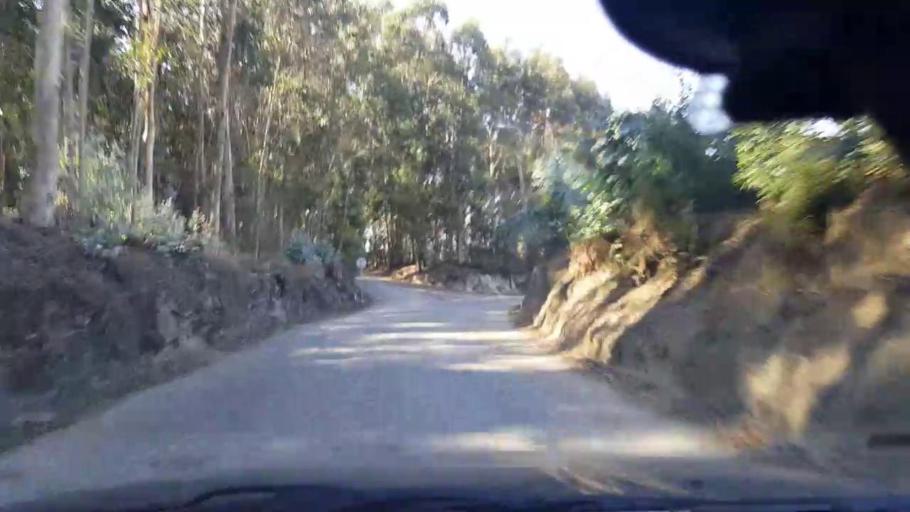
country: PT
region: Porto
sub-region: Vila do Conde
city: Arvore
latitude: 41.3558
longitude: -8.7082
